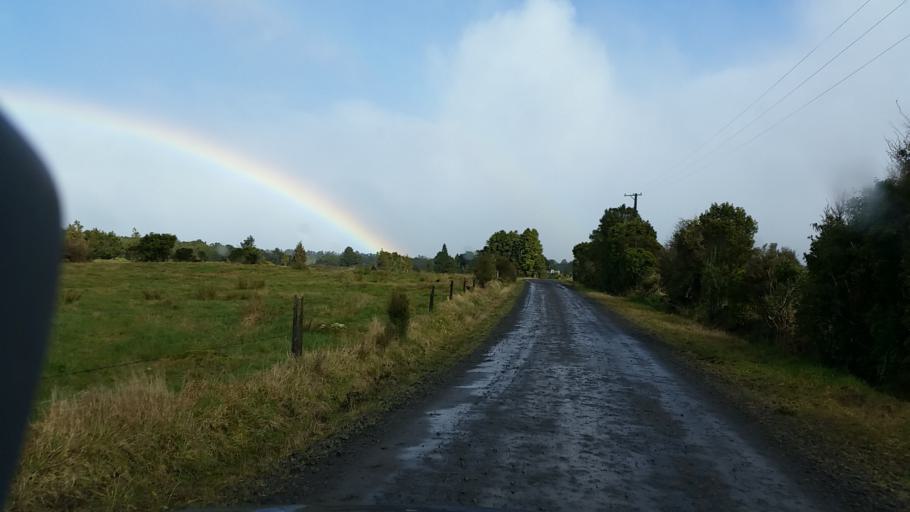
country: NZ
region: Taranaki
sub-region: South Taranaki District
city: Eltham
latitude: -39.2861
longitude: 174.1873
